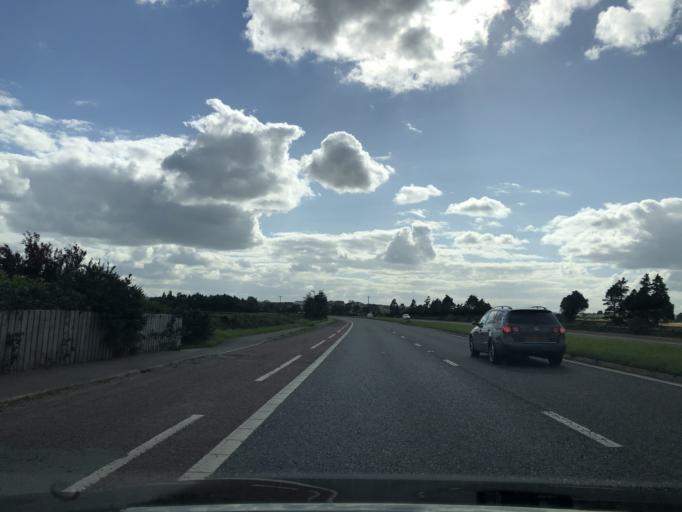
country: GB
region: Northern Ireland
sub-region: Ards District
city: Comber
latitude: 54.5587
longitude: -5.7115
